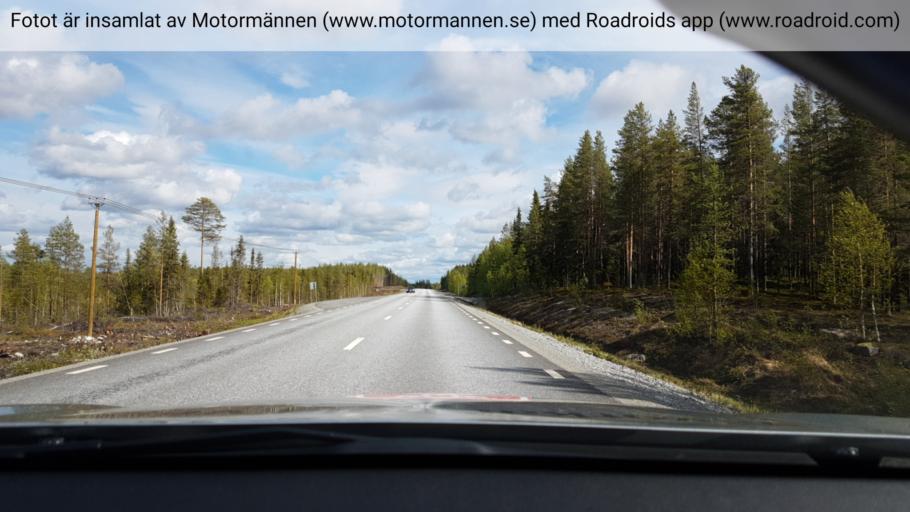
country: SE
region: Vaesternorrland
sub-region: OErnskoeldsviks Kommun
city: Bredbyn
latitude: 64.0915
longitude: 18.1936
